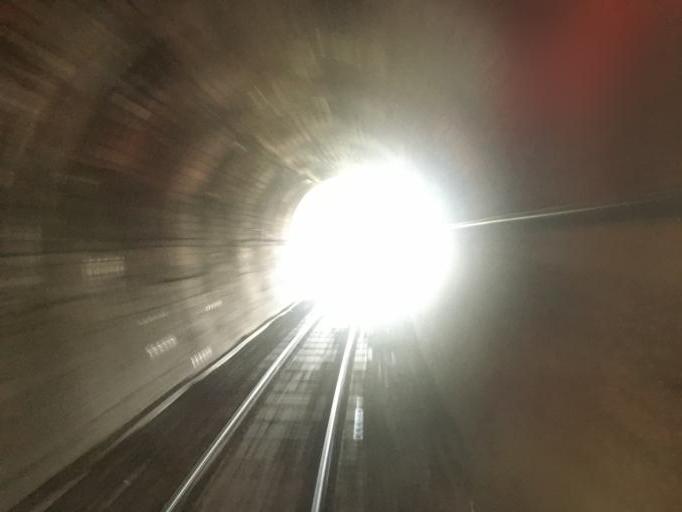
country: JP
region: Iwate
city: Ichinoseki
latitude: 38.9558
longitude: 141.2497
